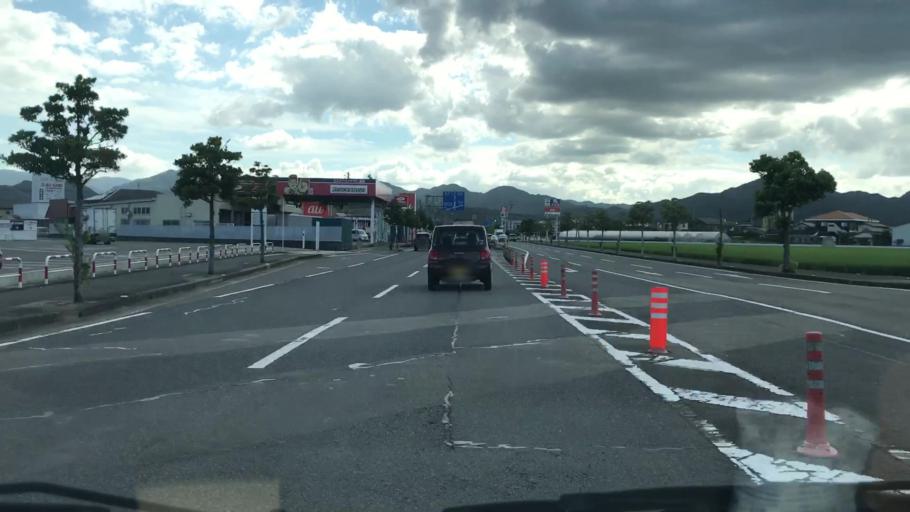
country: JP
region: Saga Prefecture
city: Kashima
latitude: 33.1237
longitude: 130.0976
